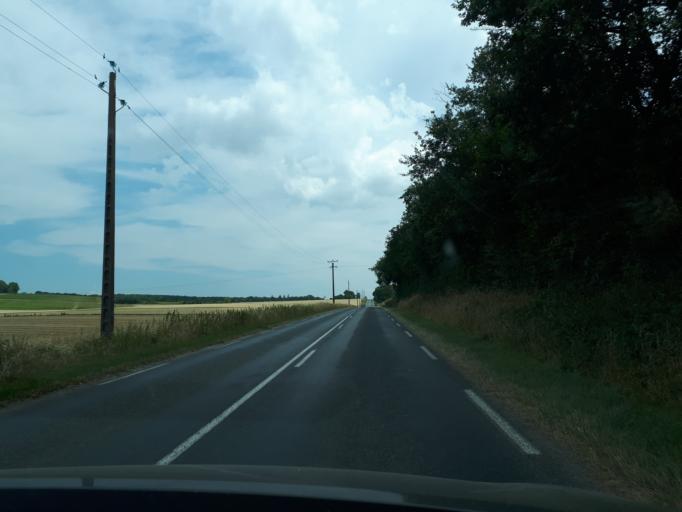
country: FR
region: Centre
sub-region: Departement du Cher
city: Rians
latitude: 47.2150
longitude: 2.6167
